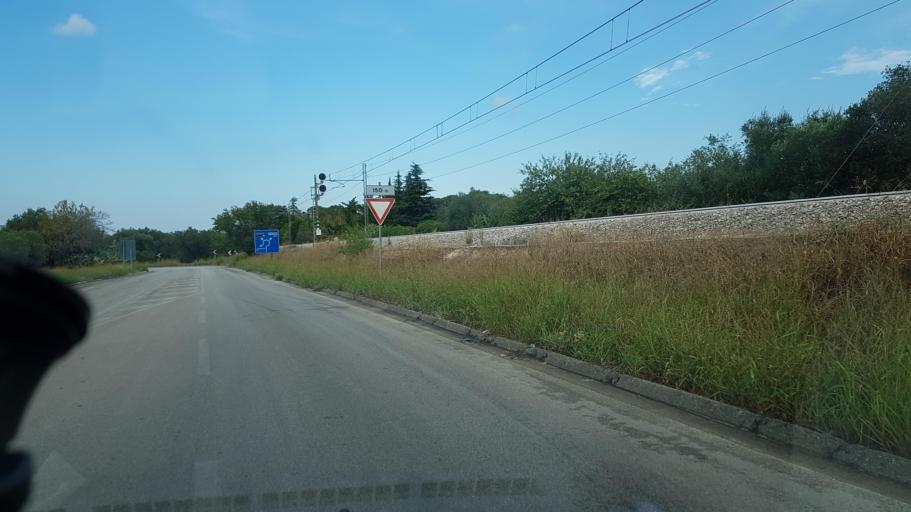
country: IT
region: Apulia
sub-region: Provincia di Brindisi
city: Latiano
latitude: 40.5465
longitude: 17.7029
